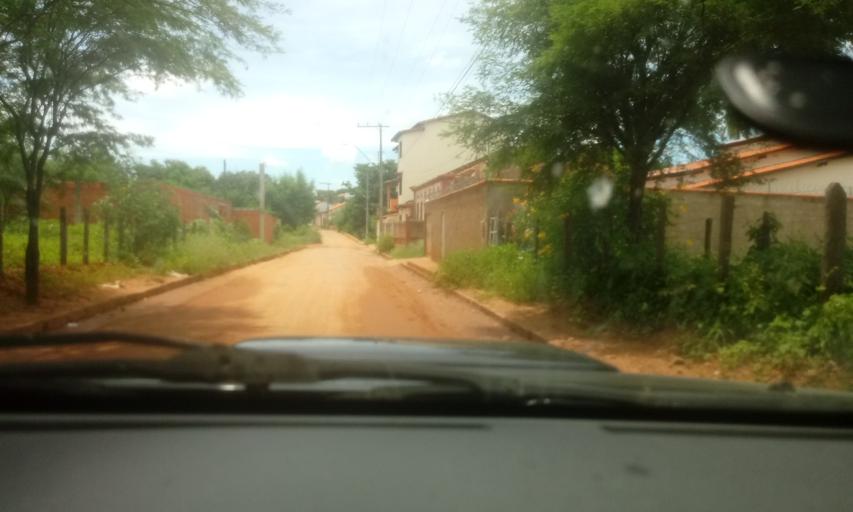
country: BR
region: Bahia
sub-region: Riacho De Santana
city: Riacho de Santana
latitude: -13.6067
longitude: -42.9448
